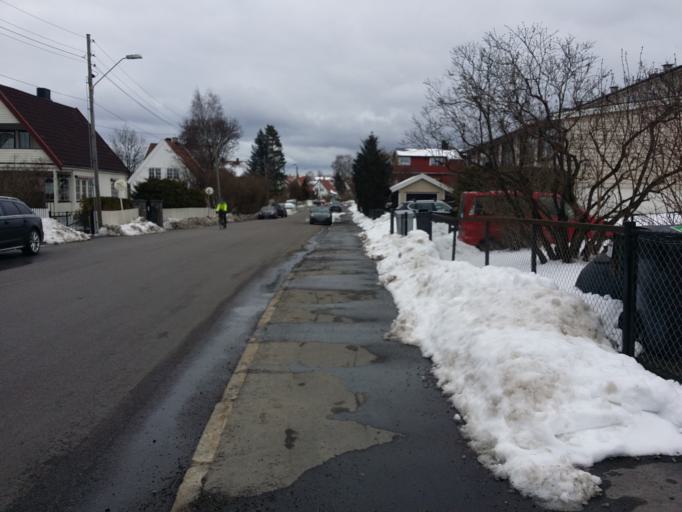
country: NO
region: Oslo
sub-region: Oslo
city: Oslo
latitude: 59.8981
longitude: 10.7766
